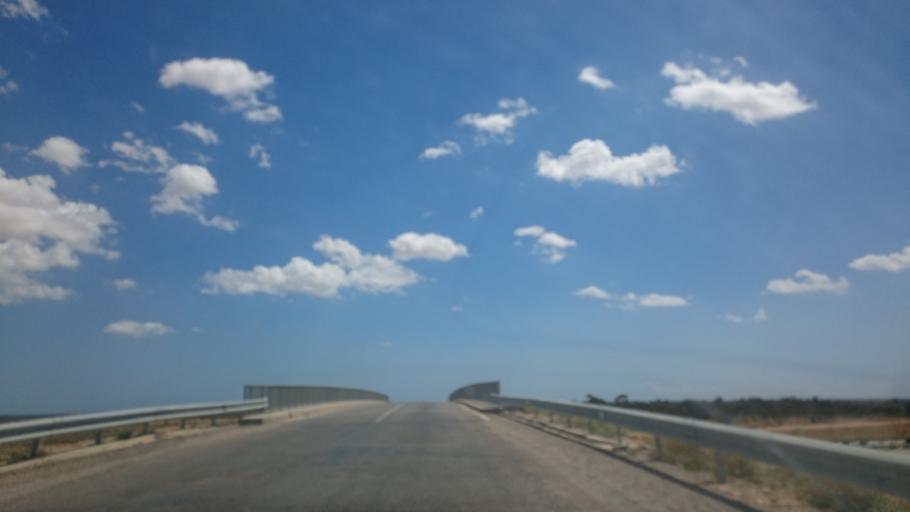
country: TN
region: Safaqis
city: Sfax
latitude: 34.6975
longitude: 10.5576
